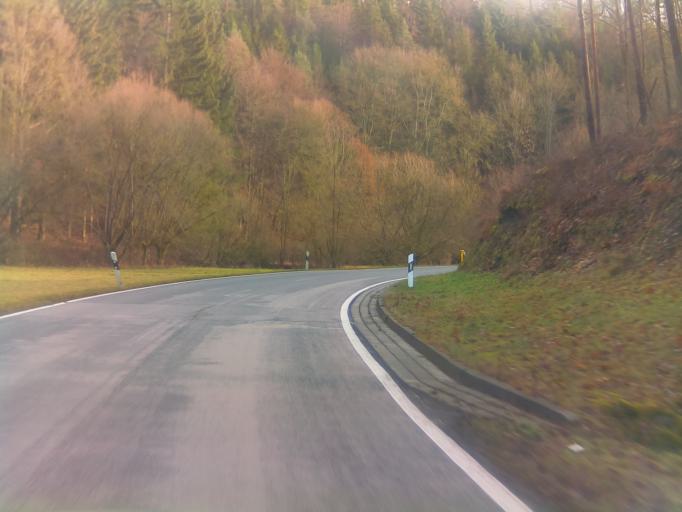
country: DE
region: Thuringia
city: Utendorf
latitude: 50.5945
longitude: 10.4445
